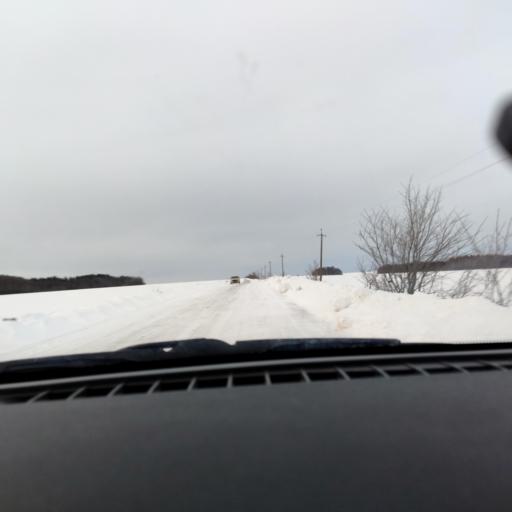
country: RU
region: Bashkortostan
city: Iglino
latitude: 54.7410
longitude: 56.5373
